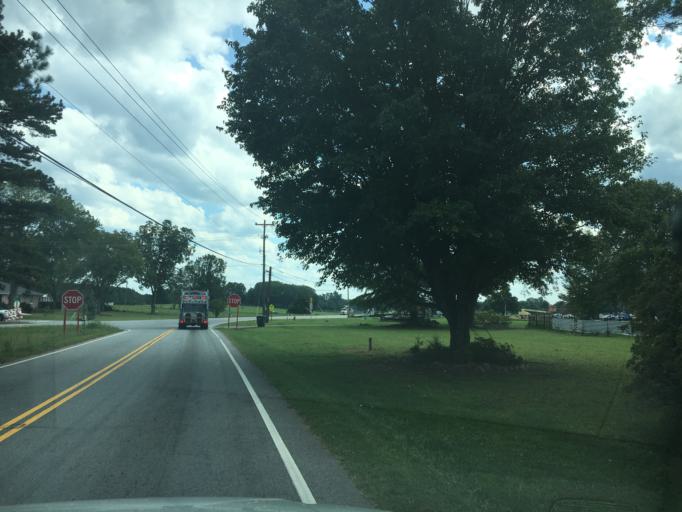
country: US
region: South Carolina
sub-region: Anderson County
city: Williamston
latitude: 34.6068
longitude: -82.4989
